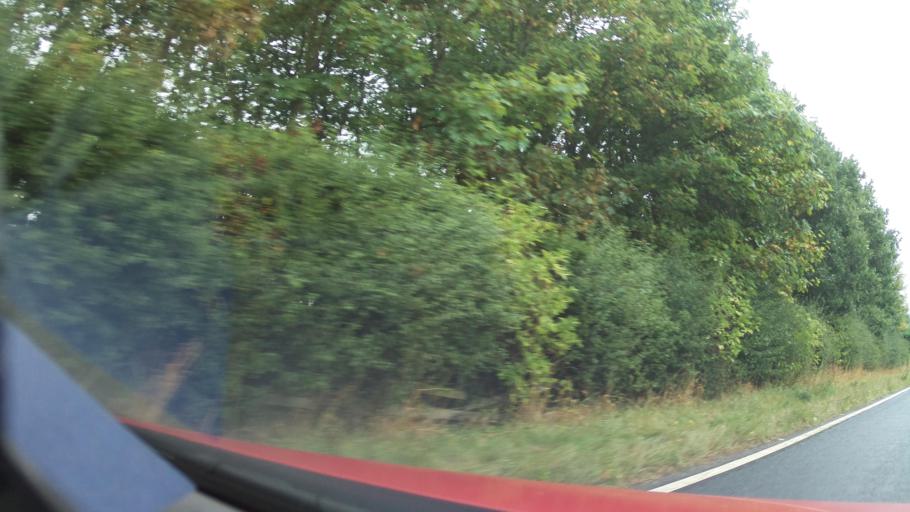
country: GB
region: England
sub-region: North Yorkshire
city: Pannal
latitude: 53.9166
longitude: -1.5284
